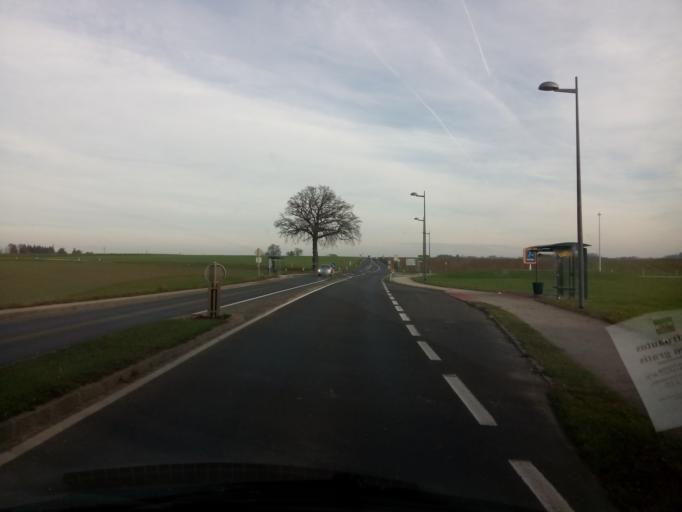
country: AT
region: Upper Austria
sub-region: Wels-Land
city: Sattledt
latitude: 48.0723
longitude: 14.0679
